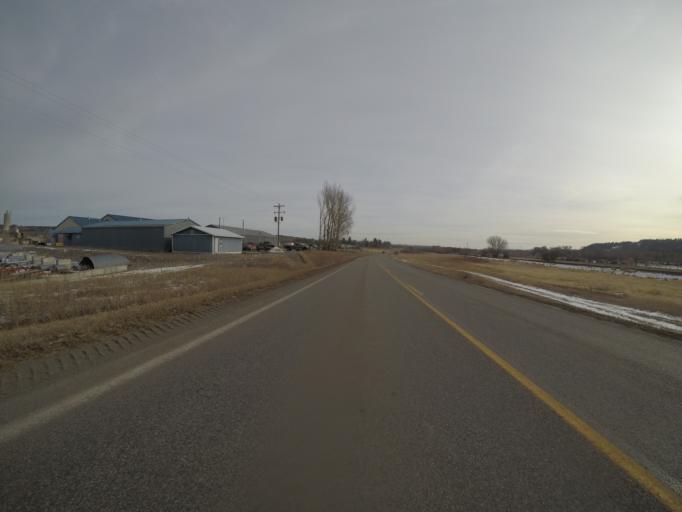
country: US
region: Montana
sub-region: Stillwater County
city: Columbus
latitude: 45.6421
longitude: -109.2821
